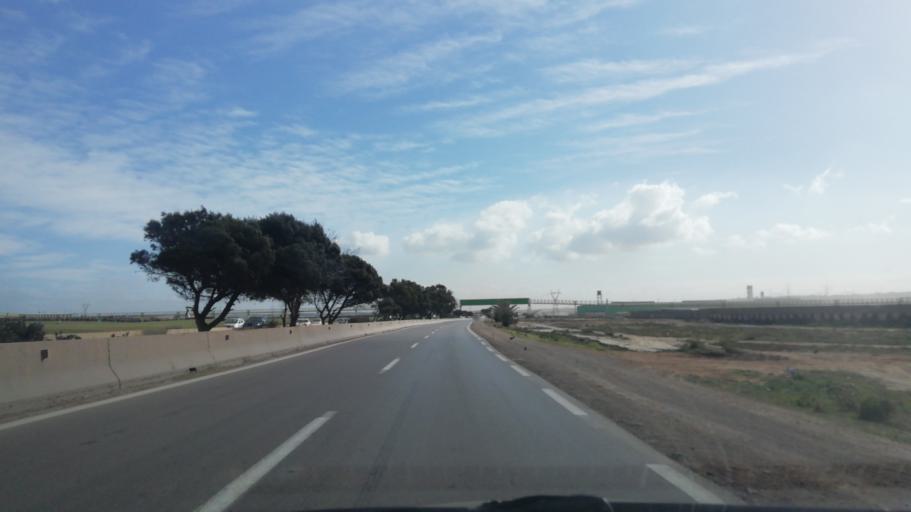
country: DZ
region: Oran
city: Ain el Bya
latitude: 35.7793
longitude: -0.2689
